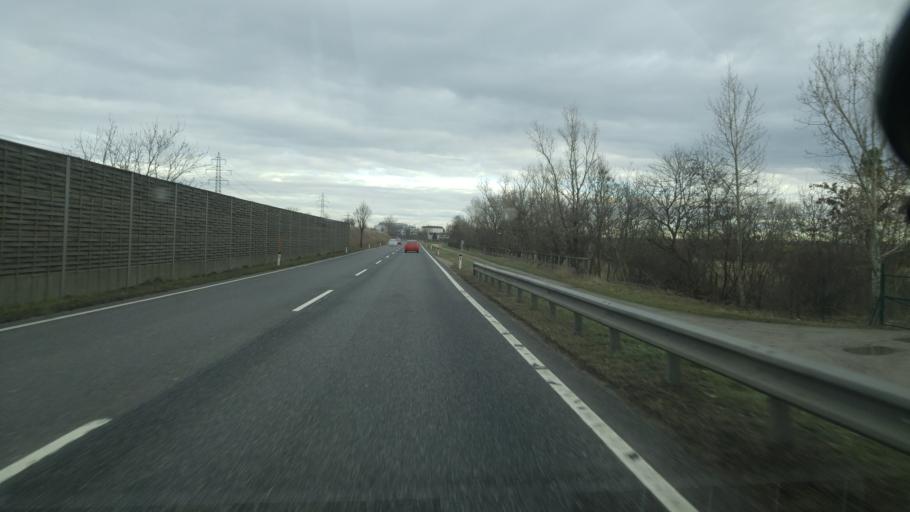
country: AT
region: Lower Austria
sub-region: Politischer Bezirk Modling
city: Biedermannsdorf
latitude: 48.0779
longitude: 16.3409
